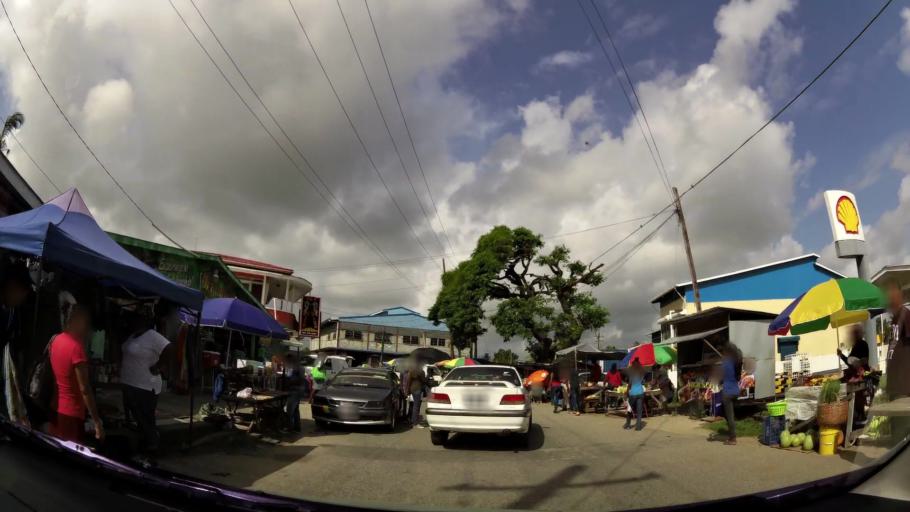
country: GY
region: Demerara-Mahaica
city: Mahaica Village
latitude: 6.6710
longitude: -57.9239
